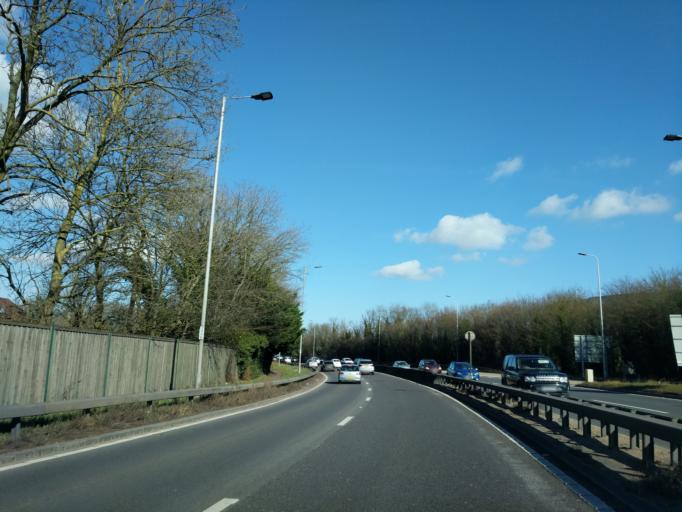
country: GB
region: England
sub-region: Surrey
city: Guildford
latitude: 51.2424
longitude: -0.5973
